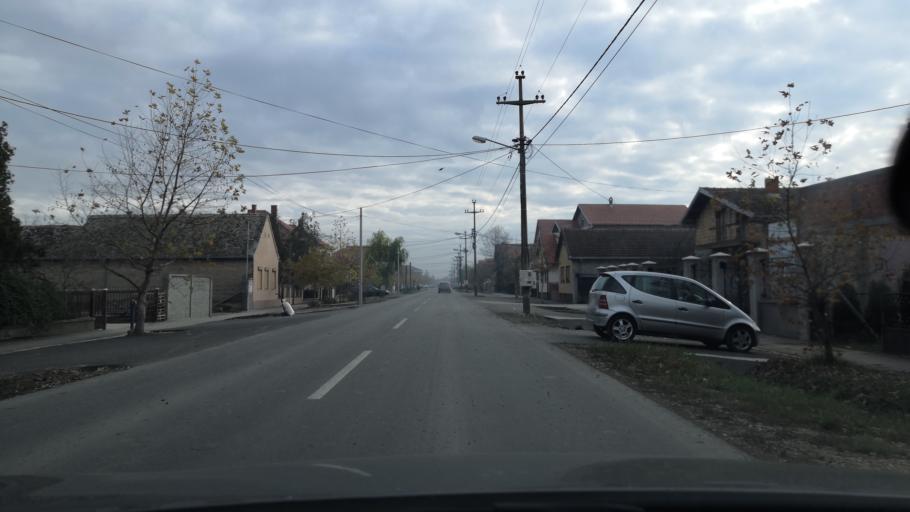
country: RS
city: Ugrinovci
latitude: 44.8744
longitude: 20.1907
